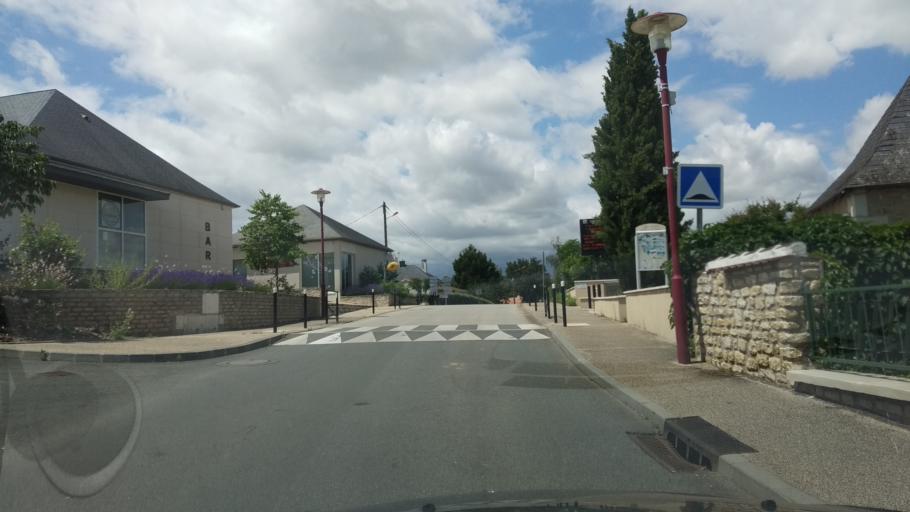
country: FR
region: Poitou-Charentes
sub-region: Departement de la Vienne
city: Cisse
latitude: 46.6074
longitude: 0.2358
